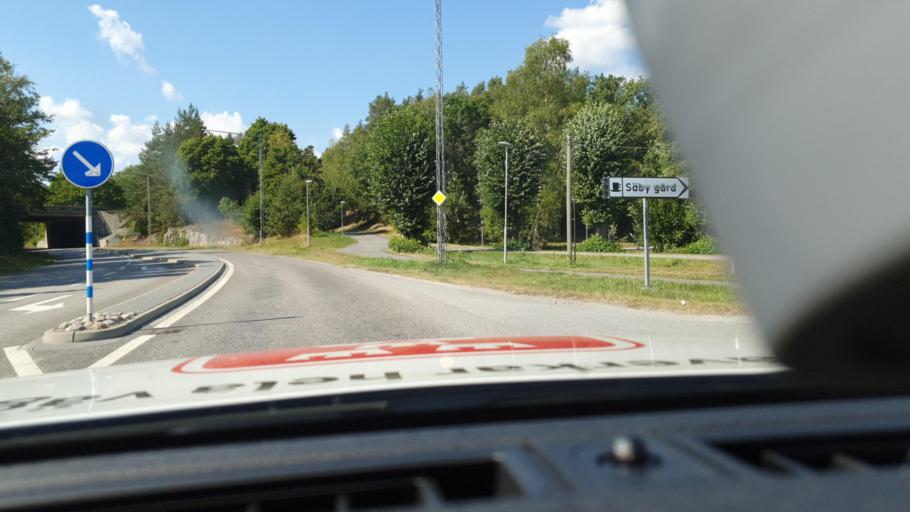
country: SE
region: Stockholm
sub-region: Jarfalla Kommun
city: Jakobsberg
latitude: 59.4254
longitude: 17.8534
